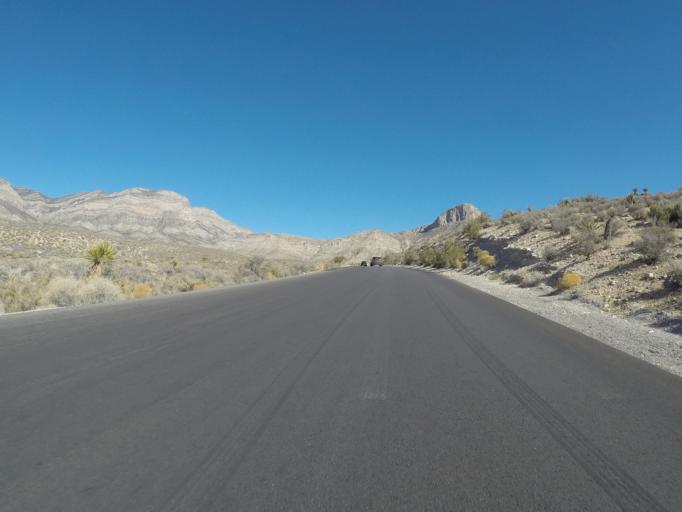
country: US
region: Nevada
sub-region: Clark County
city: Summerlin South
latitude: 36.1648
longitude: -115.4634
